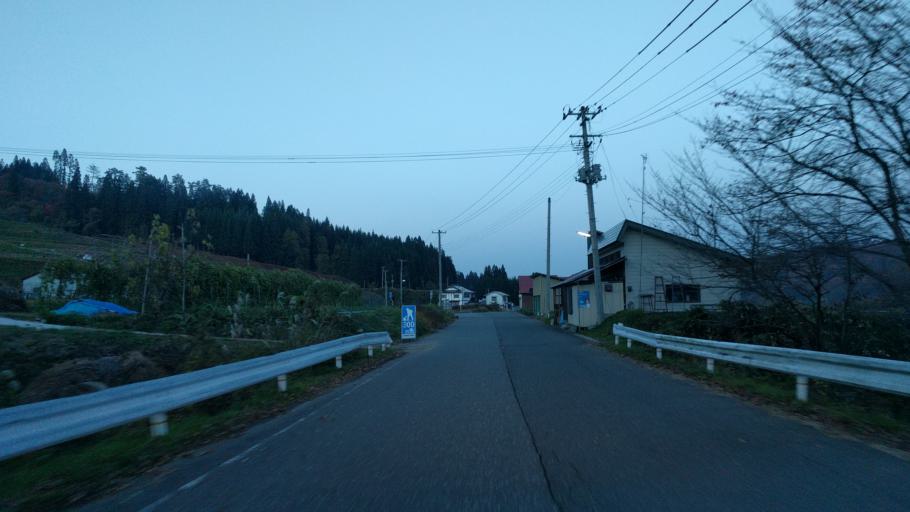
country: JP
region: Fukushima
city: Kitakata
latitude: 37.5244
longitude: 139.7116
